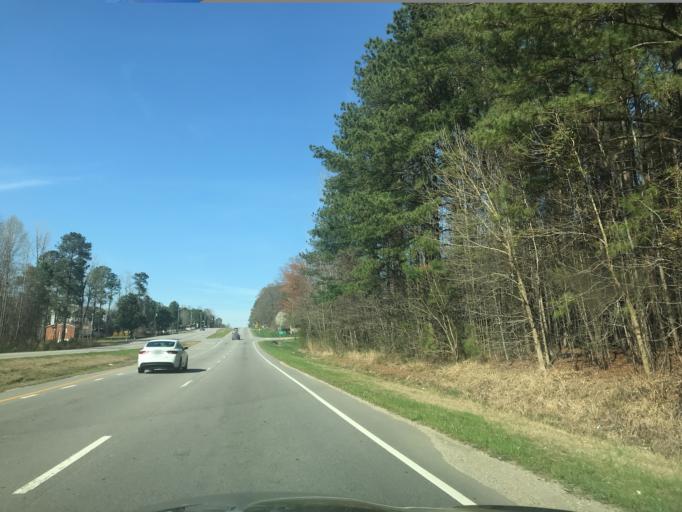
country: US
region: North Carolina
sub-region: Wake County
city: Fuquay-Varina
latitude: 35.6472
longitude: -78.7086
